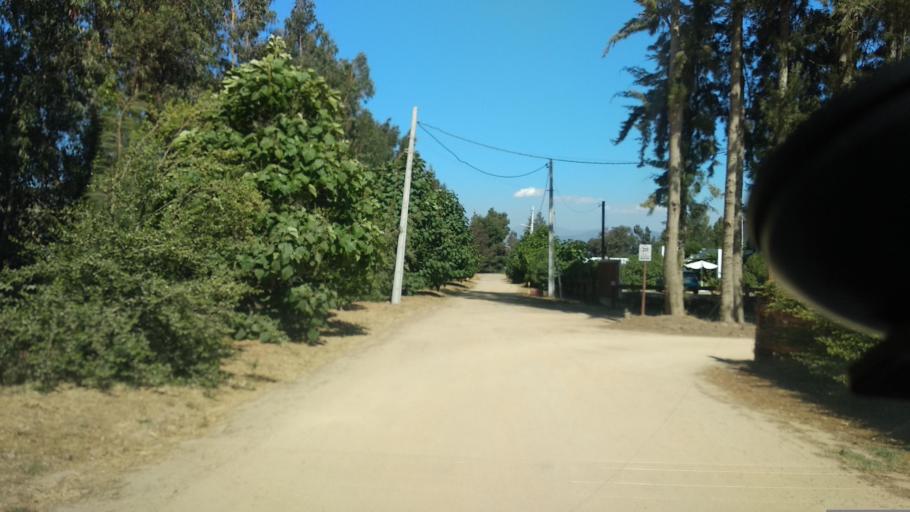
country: CL
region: Valparaiso
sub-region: Provincia de Marga Marga
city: Limache
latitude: -32.9748
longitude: -71.3093
